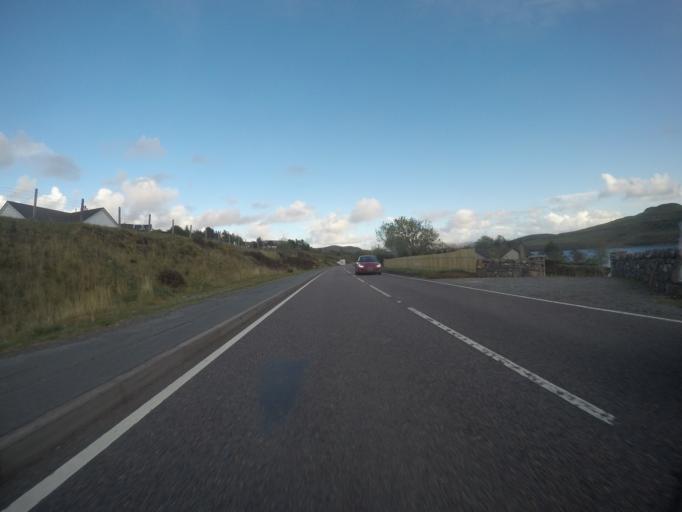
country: GB
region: Scotland
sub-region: Highland
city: Portree
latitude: 57.4886
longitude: -6.3131
